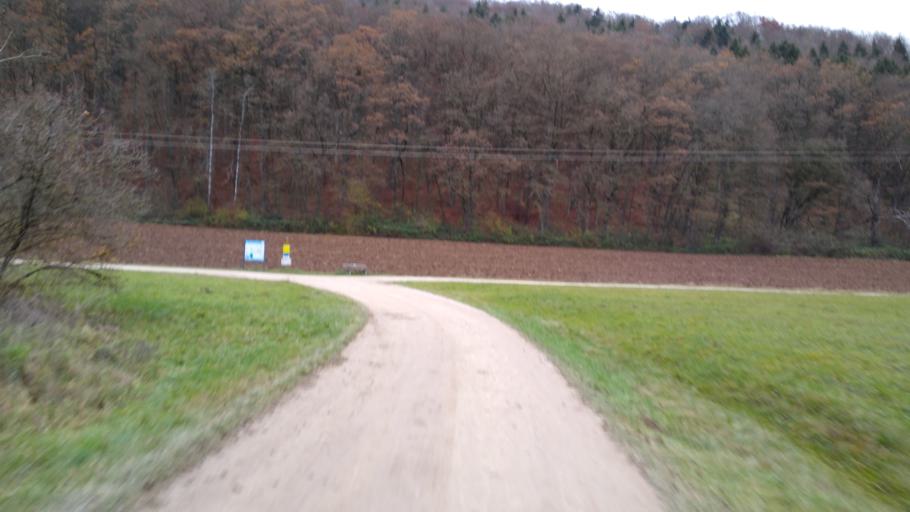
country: DE
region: Bavaria
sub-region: Upper Palatinate
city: Dietfurt
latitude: 49.0473
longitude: 11.5997
